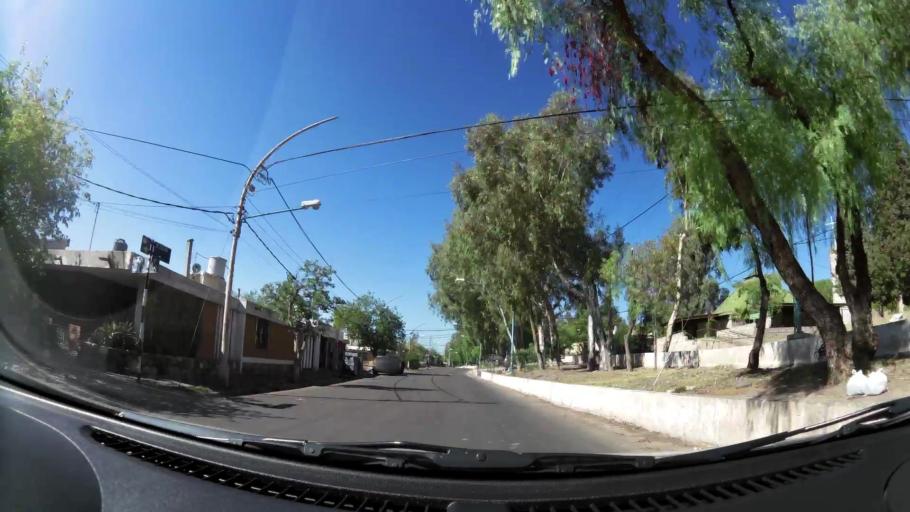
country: AR
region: Mendoza
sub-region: Departamento de Godoy Cruz
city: Godoy Cruz
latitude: -32.9019
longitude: -68.8862
